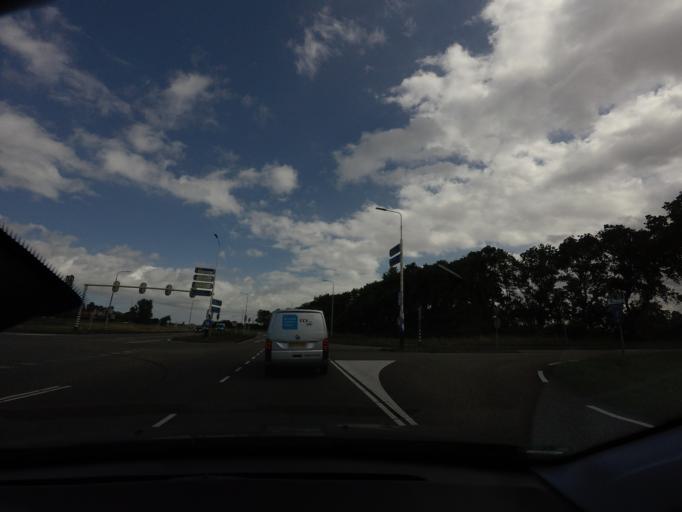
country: NL
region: North Holland
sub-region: Gemeente Den Helder
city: Den Helder
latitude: 52.9146
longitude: 4.7945
